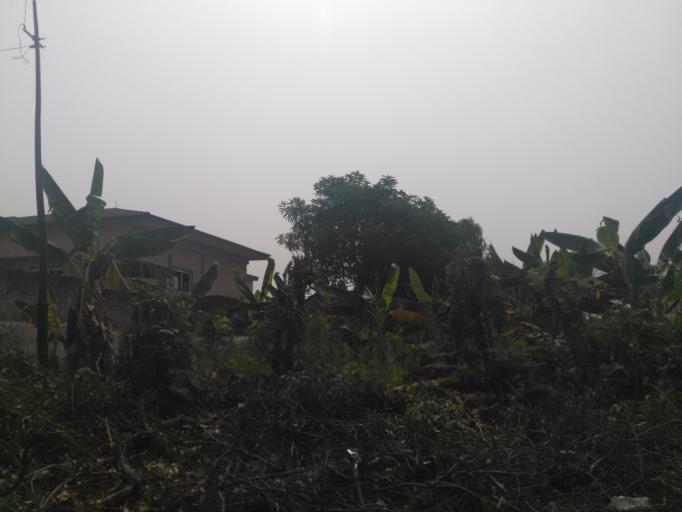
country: GH
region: Ashanti
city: Kumasi
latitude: 6.6829
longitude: -1.6344
